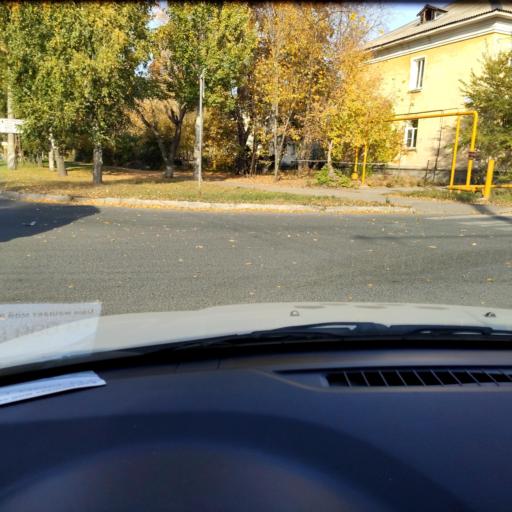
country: RU
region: Samara
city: Tol'yatti
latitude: 53.5041
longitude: 49.3906
